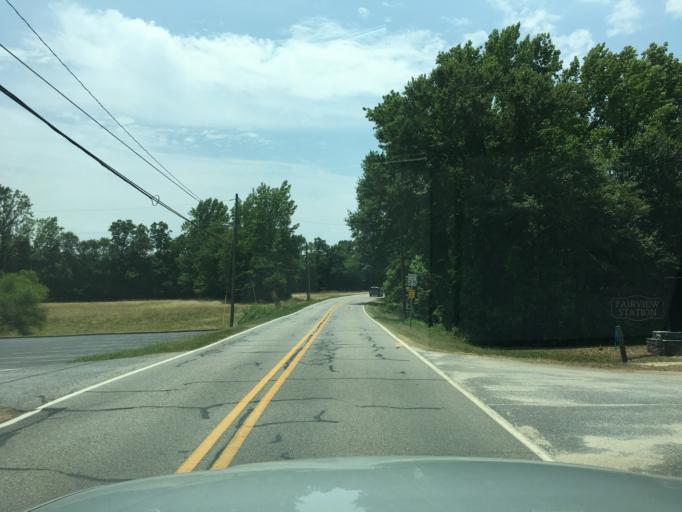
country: US
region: Georgia
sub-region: Hart County
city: Hartwell
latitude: 34.3453
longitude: -82.9192
